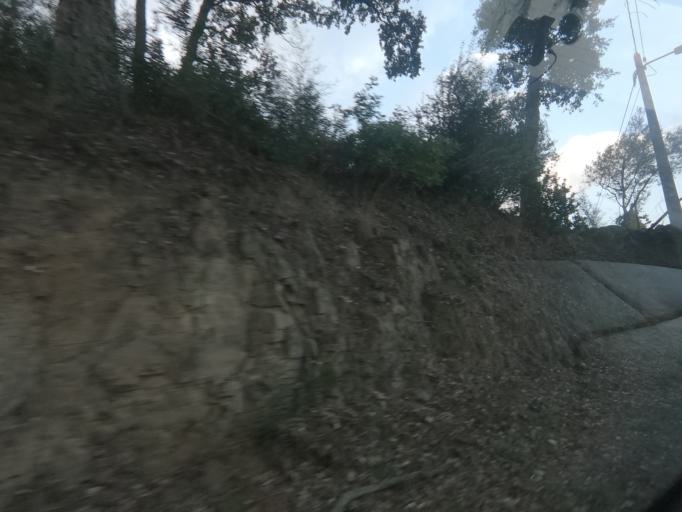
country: PT
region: Vila Real
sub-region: Mesao Frio
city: Mesao Frio
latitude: 41.1689
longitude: -7.8755
